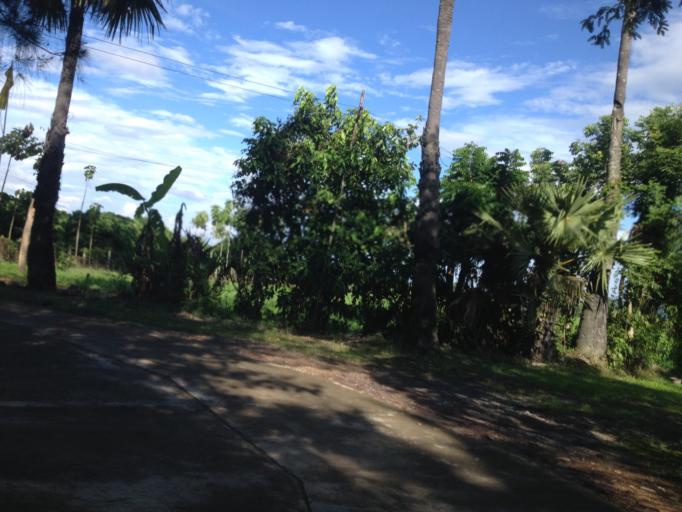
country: TH
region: Chiang Mai
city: Hang Dong
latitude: 18.6930
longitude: 98.9001
